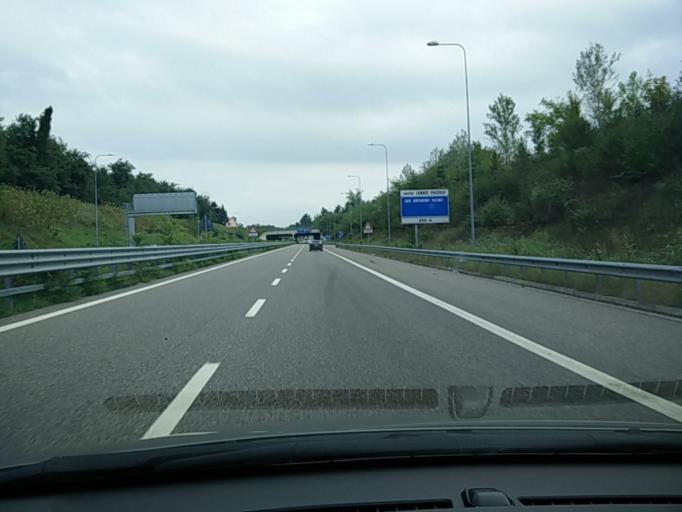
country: IT
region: Lombardy
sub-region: Provincia di Varese
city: Lonate Pozzolo
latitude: 45.5755
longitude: 8.7358
